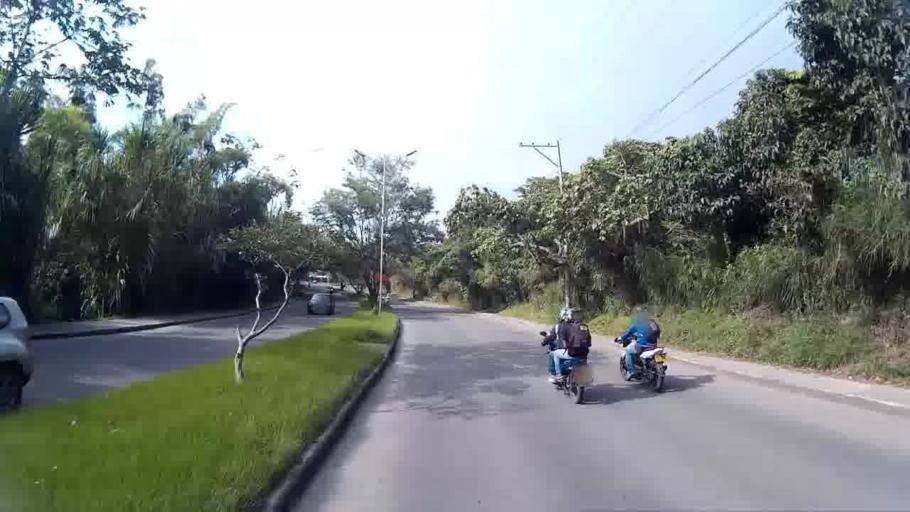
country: CO
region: Quindio
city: Calarca
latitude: 4.5487
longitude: -75.6544
